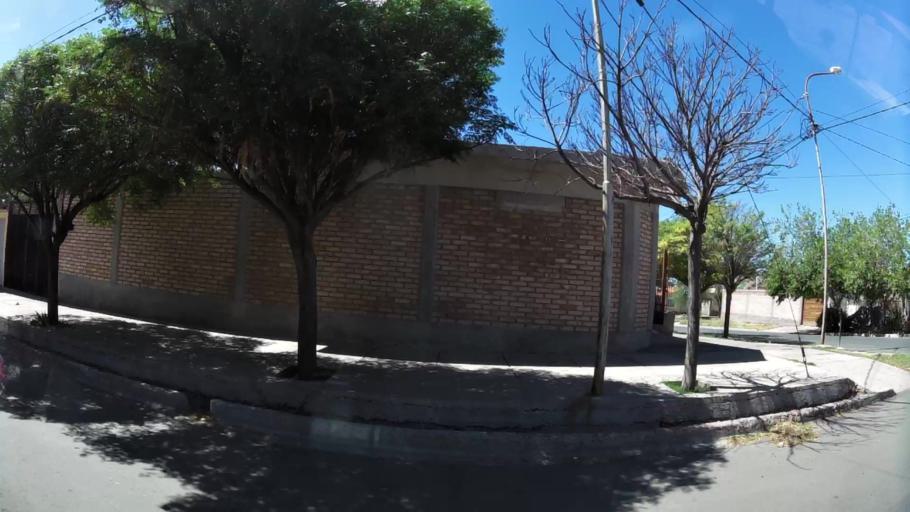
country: AR
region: Mendoza
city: Las Heras
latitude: -32.8456
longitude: -68.8743
